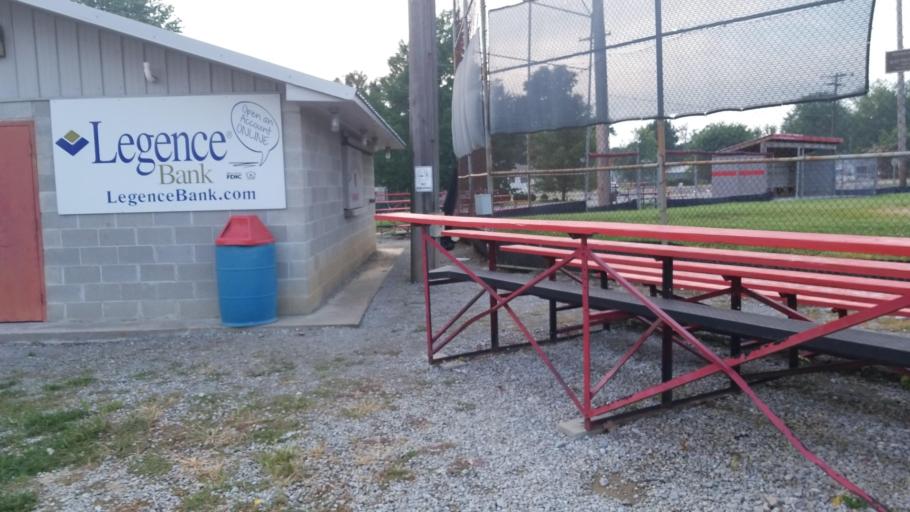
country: US
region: Illinois
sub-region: Saline County
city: Harrisburg
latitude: 37.8414
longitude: -88.6051
